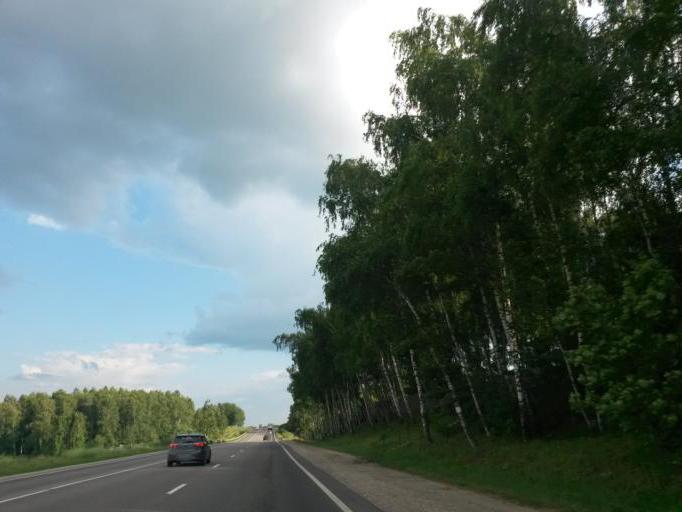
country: RU
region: Moskovskaya
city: Barybino
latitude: 55.2671
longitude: 37.8286
